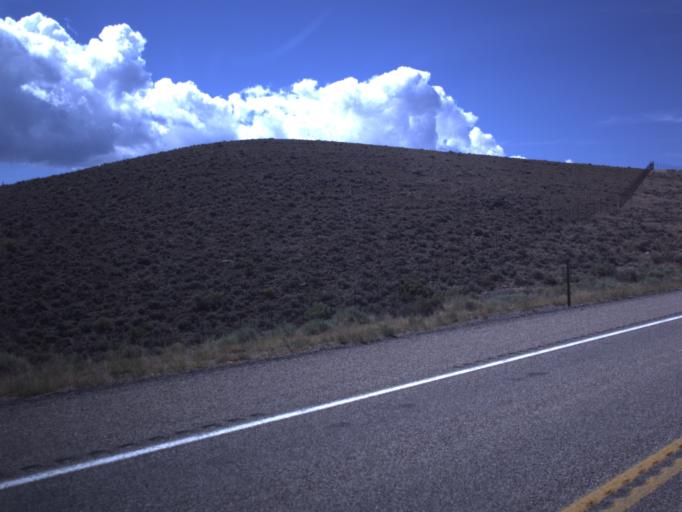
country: US
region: Utah
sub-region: Piute County
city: Junction
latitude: 38.2153
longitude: -112.2208
